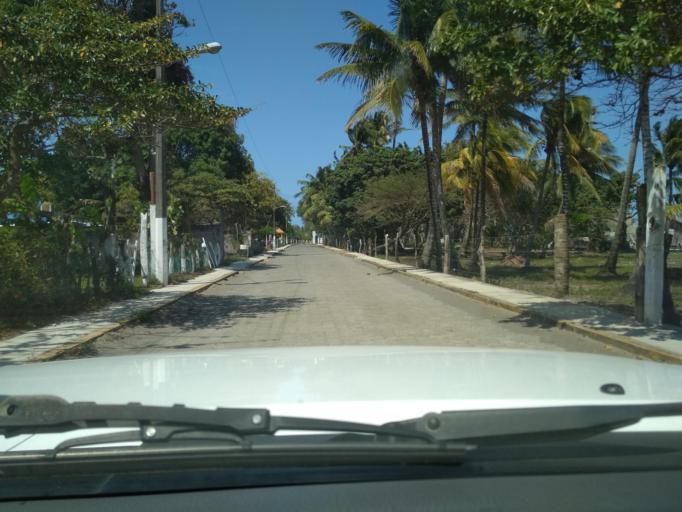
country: MX
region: Veracruz
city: Anton Lizardo
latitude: 19.0130
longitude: -95.9675
